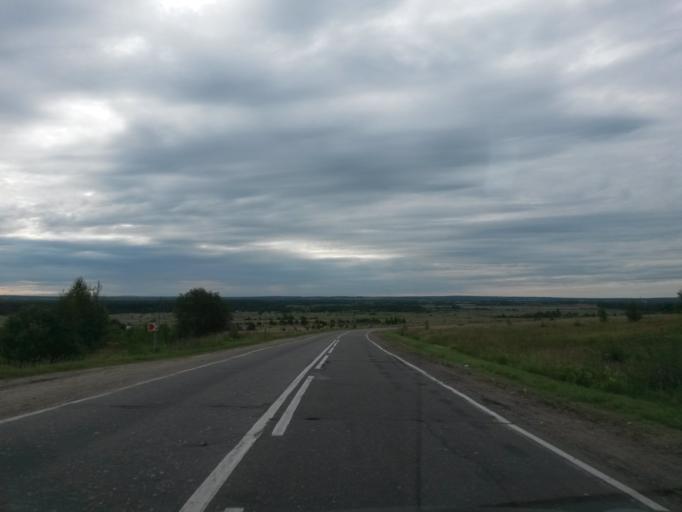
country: RU
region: Jaroslavl
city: Gavrilov-Yam
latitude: 57.3595
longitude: 39.7788
